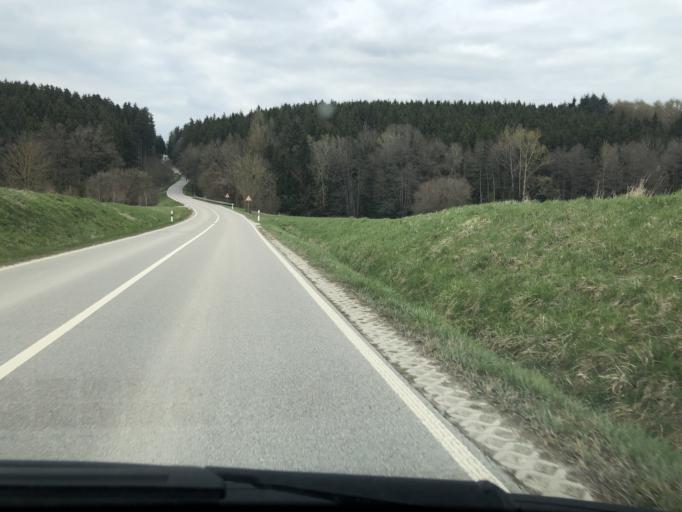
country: DE
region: Bavaria
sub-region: Upper Bavaria
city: Wolfersdorf
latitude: 48.4657
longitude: 11.7056
